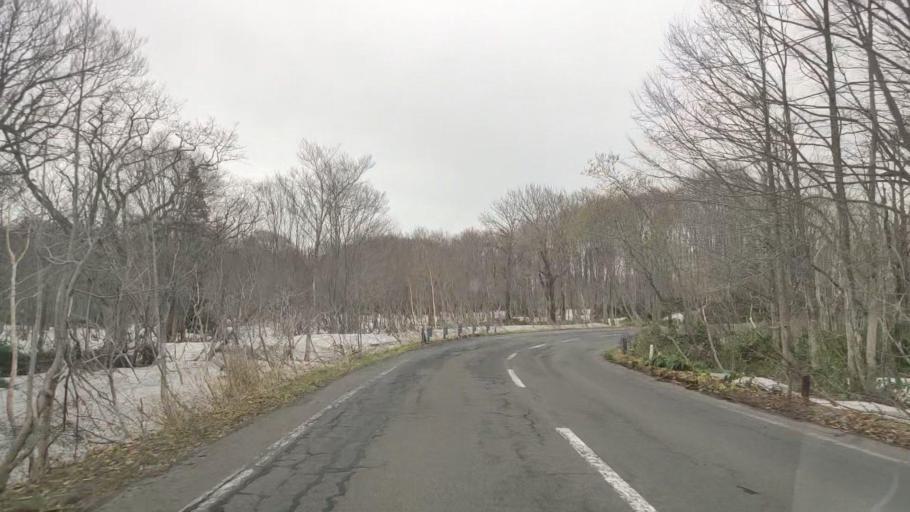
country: JP
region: Aomori
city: Aomori Shi
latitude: 40.6321
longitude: 140.9290
